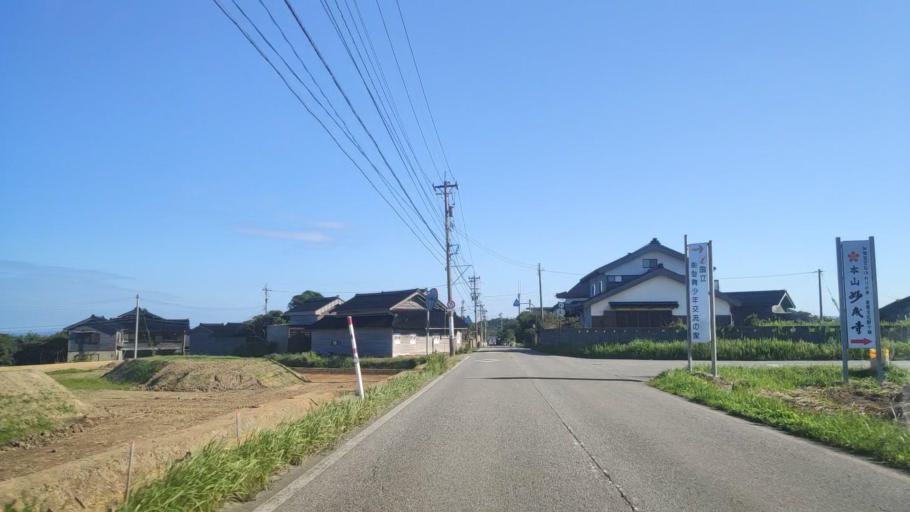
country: JP
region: Ishikawa
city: Hakui
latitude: 36.9419
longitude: 136.7619
